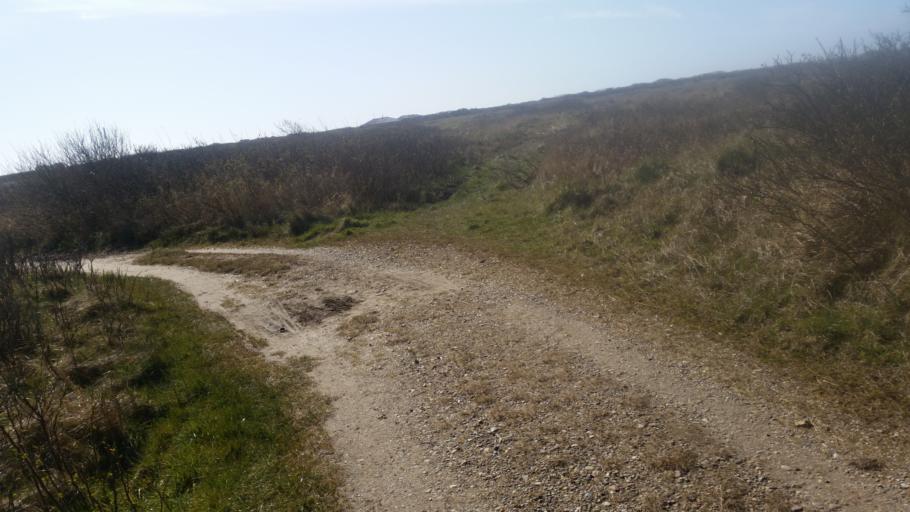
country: DE
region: Schleswig-Holstein
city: List
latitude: 55.1510
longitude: 8.4973
